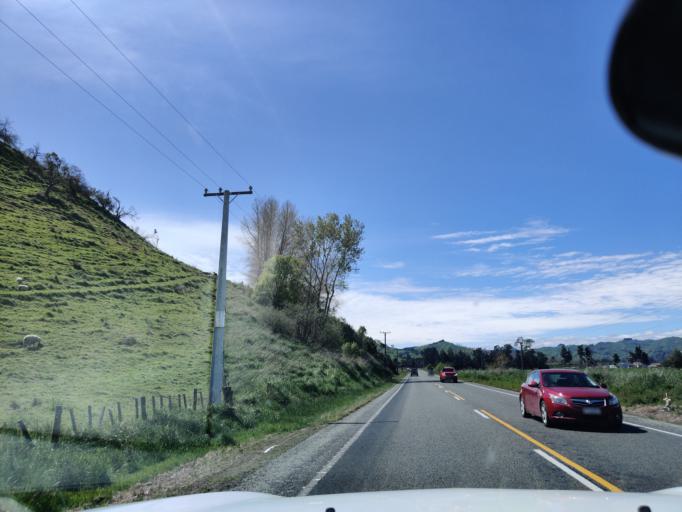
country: NZ
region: Manawatu-Wanganui
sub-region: Ruapehu District
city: Waiouru
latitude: -39.8505
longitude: 175.7330
